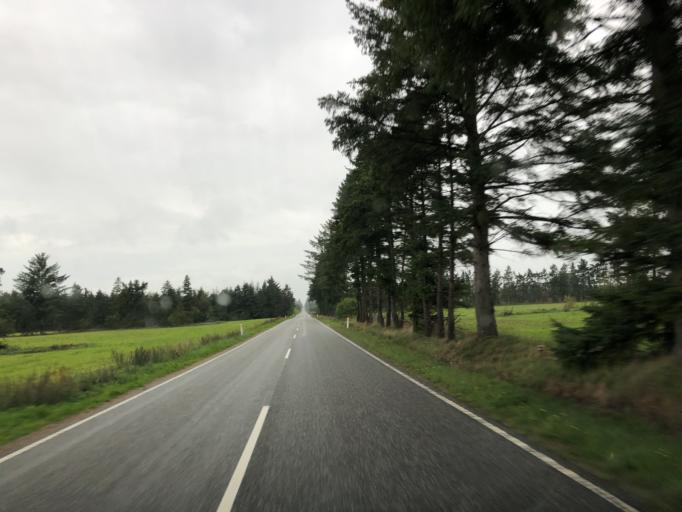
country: DK
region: South Denmark
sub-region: Vejle Kommune
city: Give
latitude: 55.9844
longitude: 9.2632
